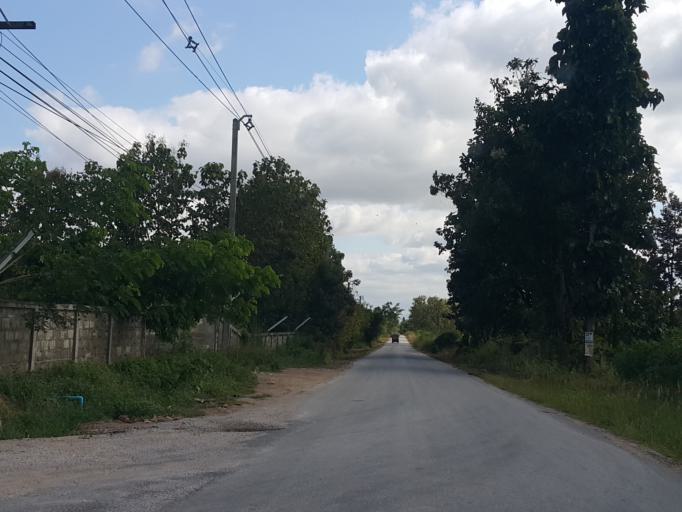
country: TH
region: Lampang
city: Hang Chat
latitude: 18.3417
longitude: 99.3783
